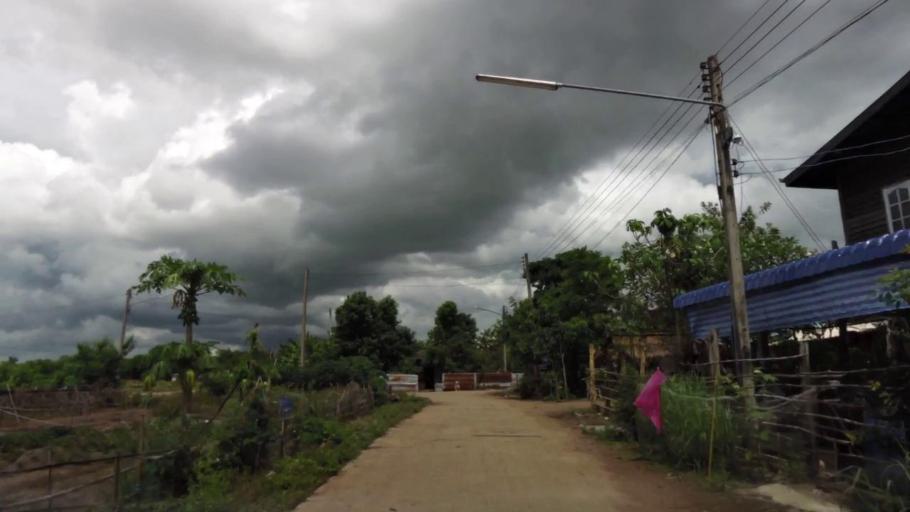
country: TH
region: Nakhon Sawan
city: Phai Sali
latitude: 15.6060
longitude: 100.6555
